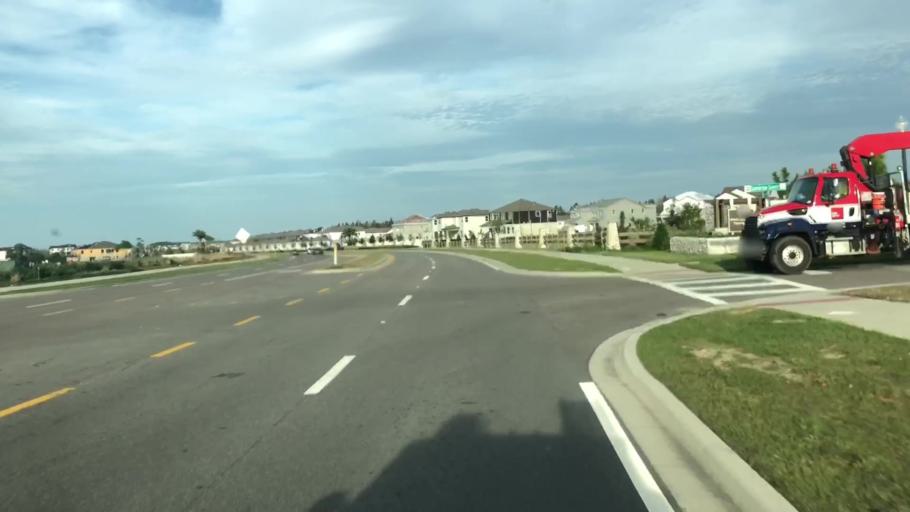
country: US
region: Florida
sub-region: Polk County
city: Citrus Ridge
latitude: 28.4205
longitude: -81.6238
